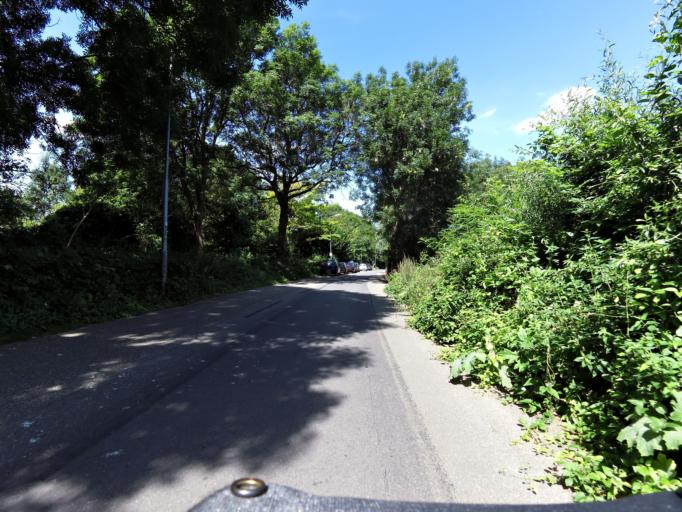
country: NL
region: South Holland
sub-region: Gemeente Rotterdam
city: Delfshaven
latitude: 51.8750
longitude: 4.4561
